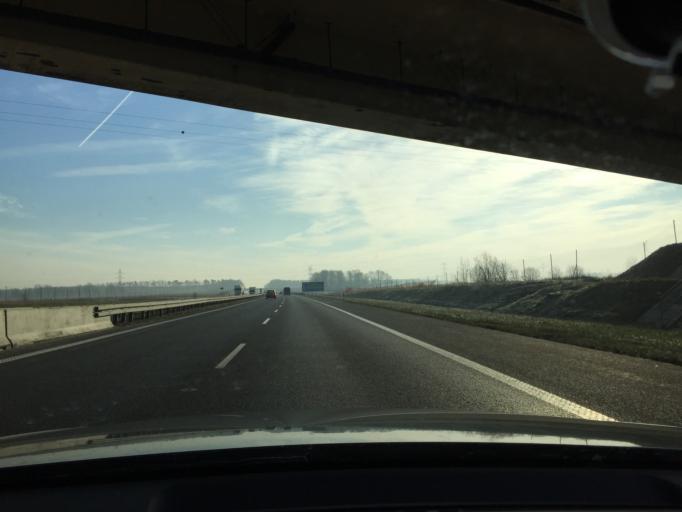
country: PL
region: Silesian Voivodeship
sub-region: Powiat gliwicki
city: Sosnicowice
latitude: 50.2995
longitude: 18.5559
